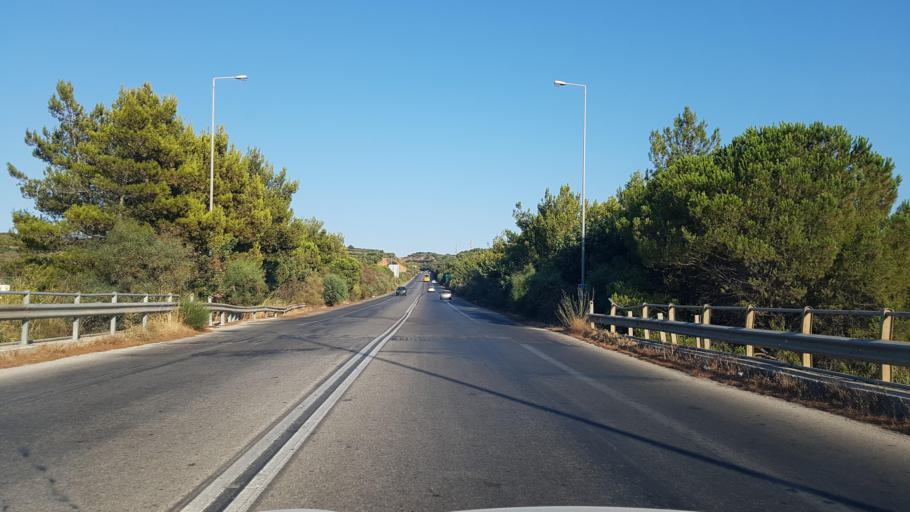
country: GR
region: Crete
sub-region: Nomos Chanias
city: Kolympari
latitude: 35.5184
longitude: 23.8217
